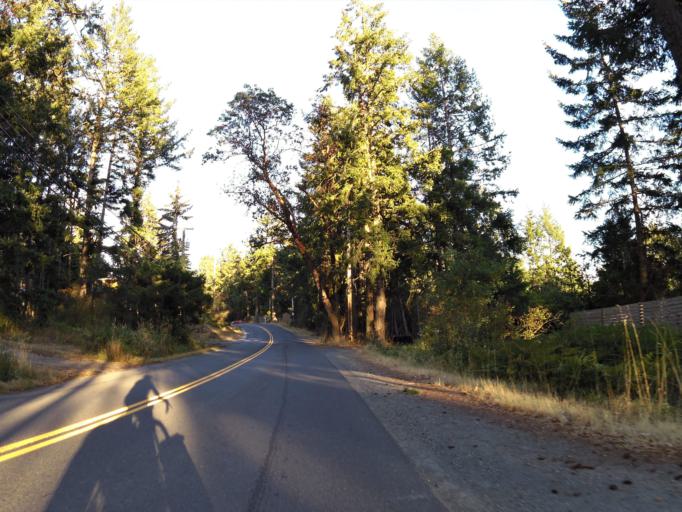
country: CA
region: British Columbia
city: North Cowichan
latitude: 48.8789
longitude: -123.5617
